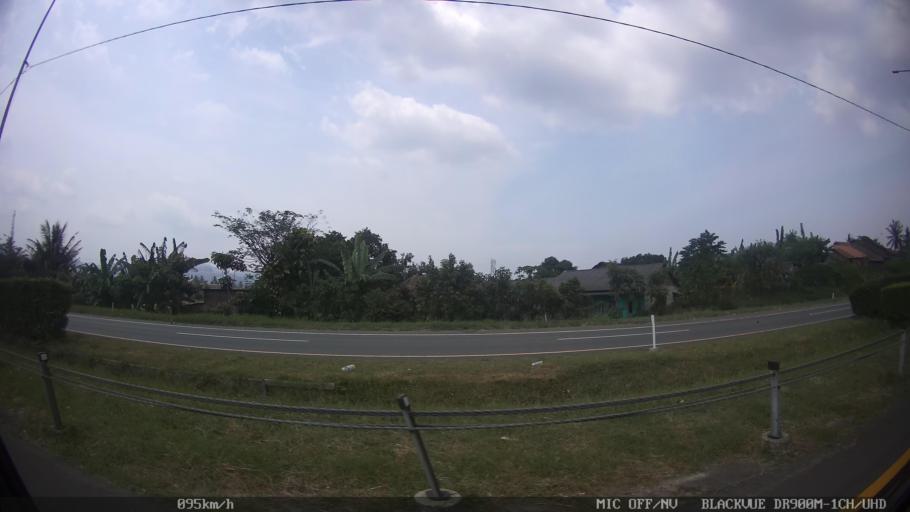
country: ID
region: Banten
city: Curug
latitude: -5.9930
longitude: 106.0529
